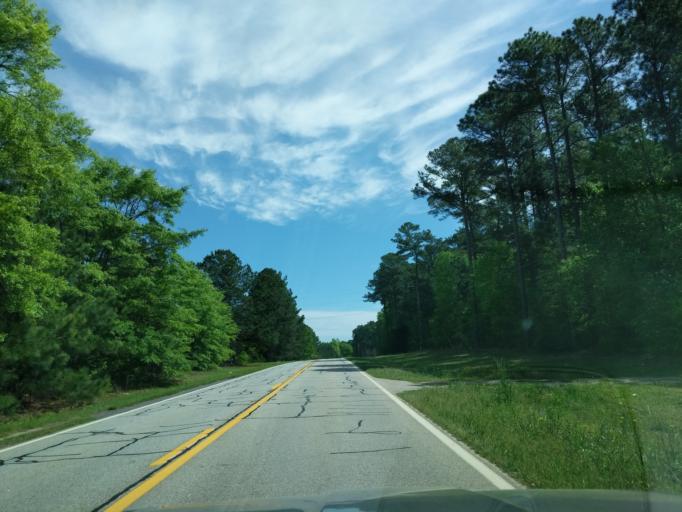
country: US
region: Georgia
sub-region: Columbia County
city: Appling
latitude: 33.6108
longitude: -82.3671
